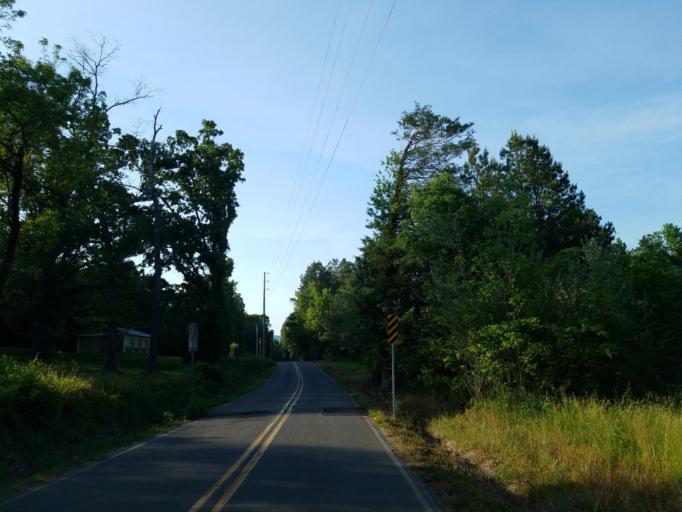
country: US
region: Georgia
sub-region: Gordon County
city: Calhoun
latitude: 34.4967
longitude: -85.1143
